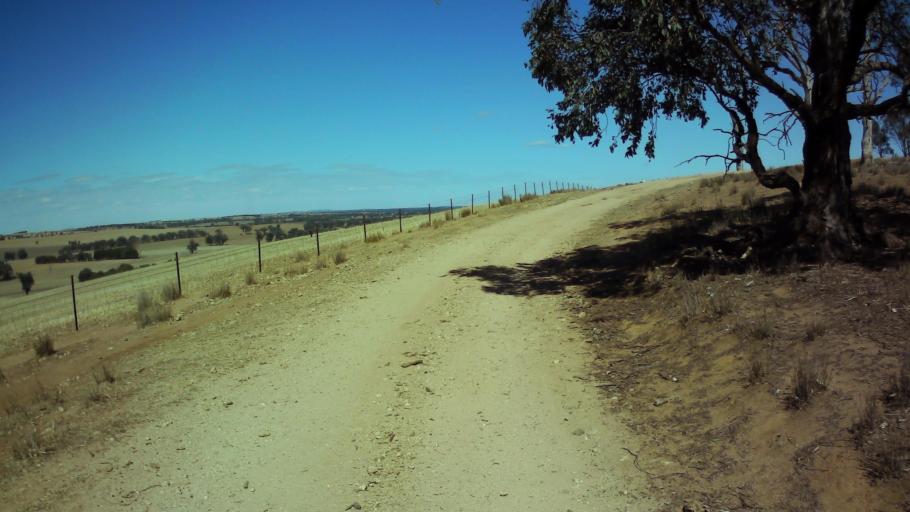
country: AU
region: New South Wales
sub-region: Weddin
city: Grenfell
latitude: -33.9964
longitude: 148.4369
